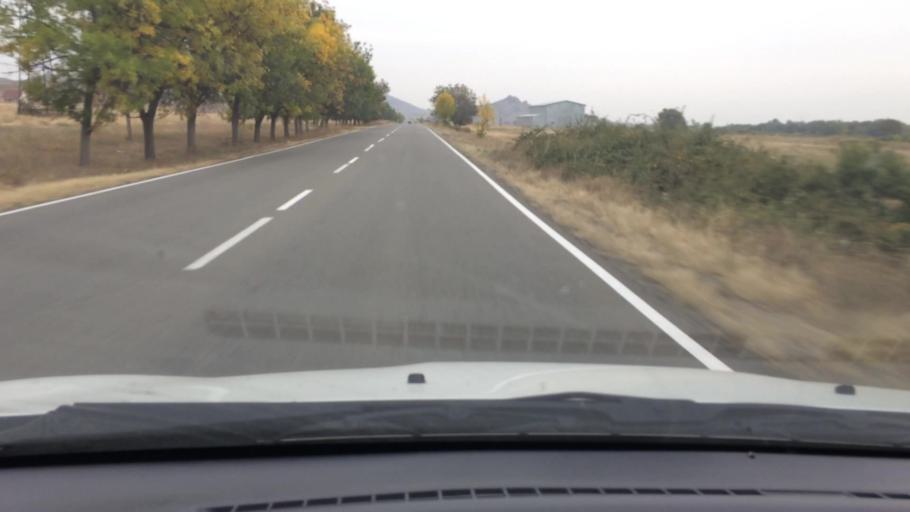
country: GE
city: Naghvarevi
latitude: 41.3353
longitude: 44.8079
